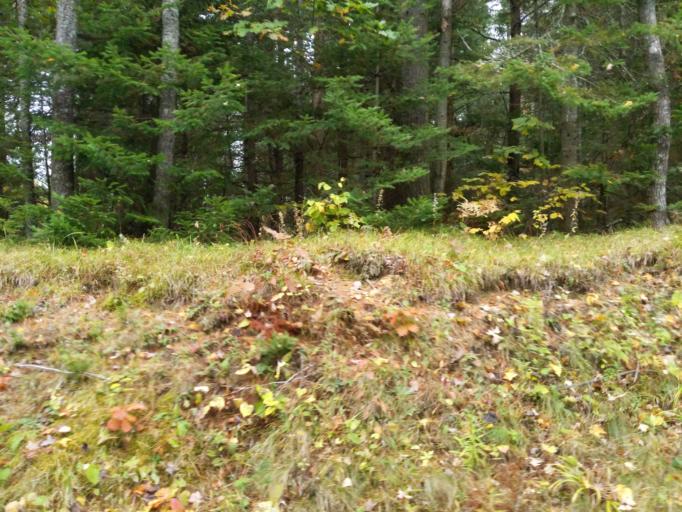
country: US
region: Maine
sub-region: Lincoln County
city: Wiscasset
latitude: 44.0730
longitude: -69.6215
